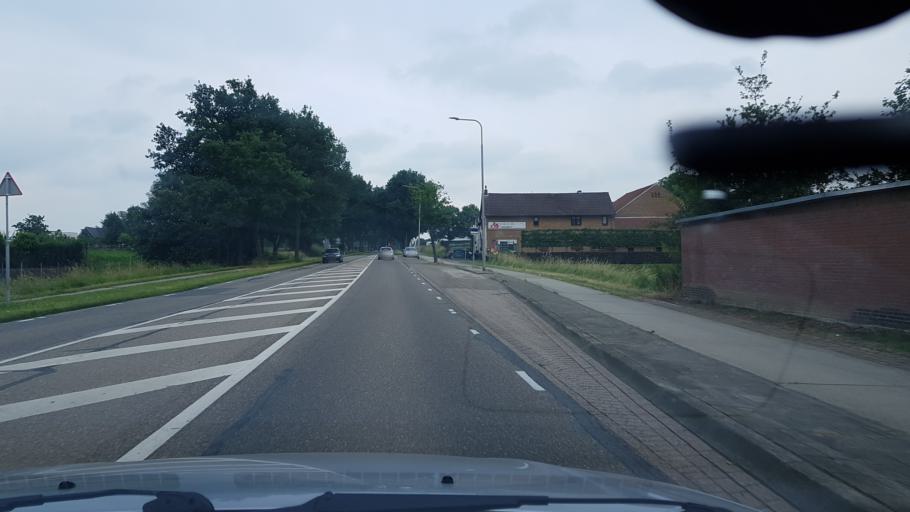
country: NL
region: Limburg
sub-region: Gemeente Schinnen
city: Oirsbeek
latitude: 50.9588
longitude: 5.9084
